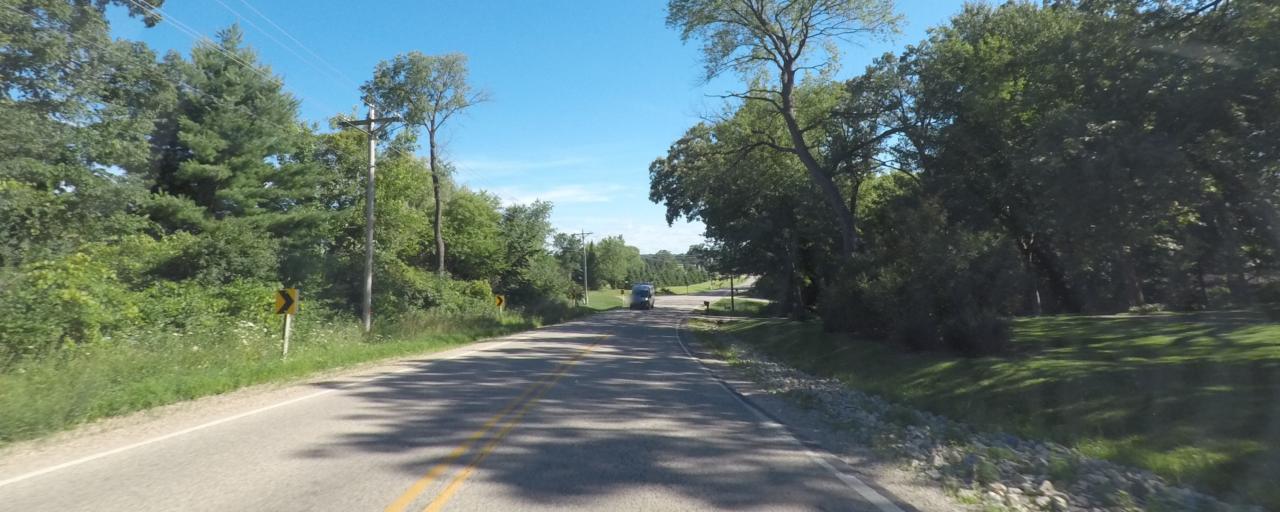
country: US
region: Wisconsin
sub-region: Rock County
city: Edgerton
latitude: 42.7423
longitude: -89.1304
